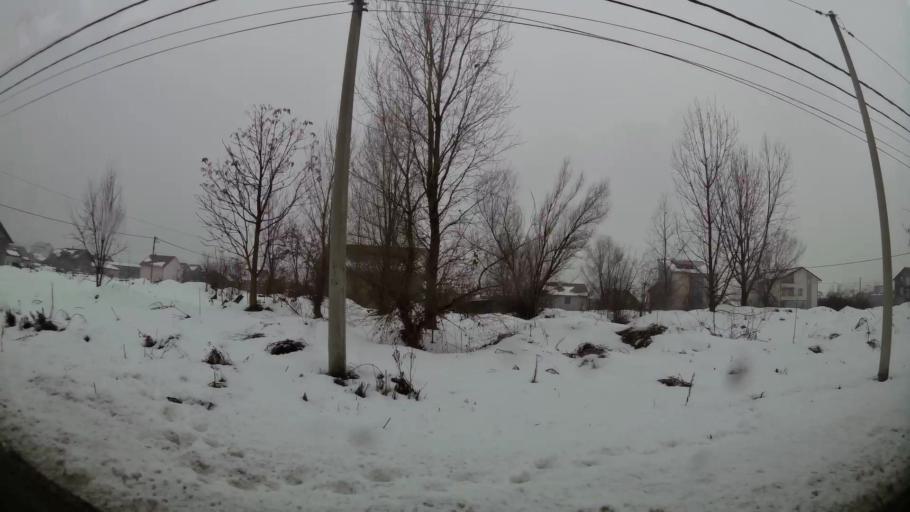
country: RS
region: Central Serbia
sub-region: Belgrade
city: Zemun
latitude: 44.8563
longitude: 20.3423
